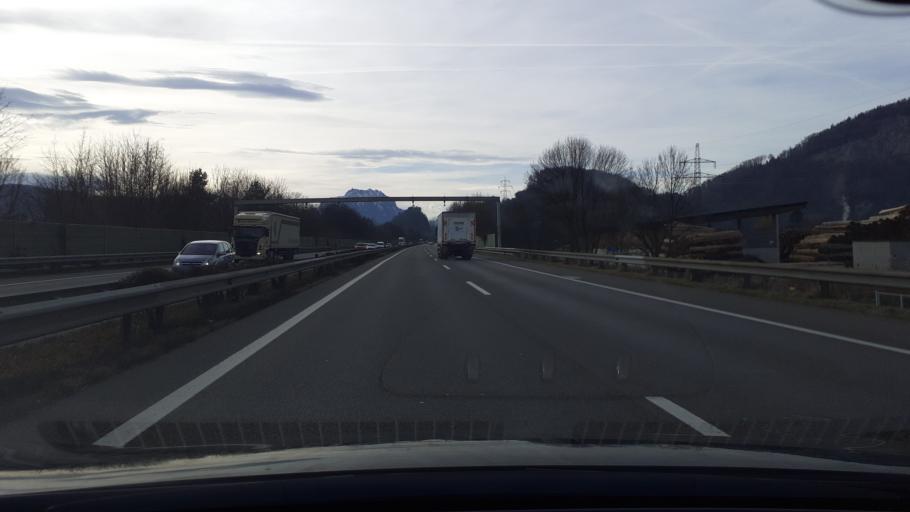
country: AT
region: Vorarlberg
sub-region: Politischer Bezirk Feldkirch
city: Gotzis
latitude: 47.3446
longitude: 9.6349
